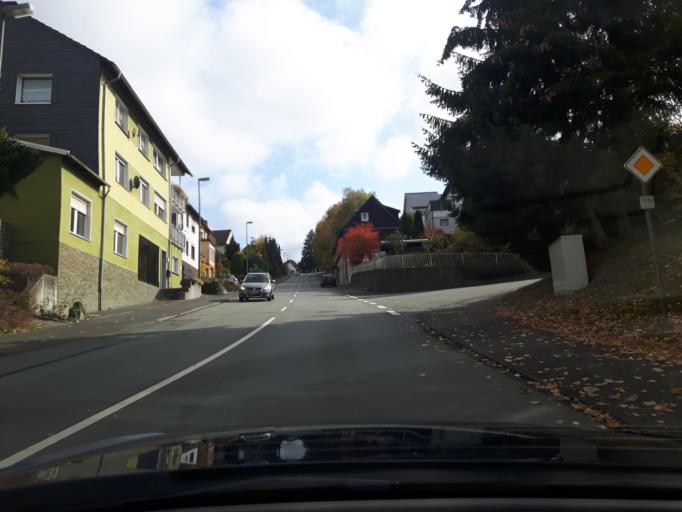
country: DE
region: North Rhine-Westphalia
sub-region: Regierungsbezirk Arnsberg
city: Bad Berleburg
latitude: 51.0453
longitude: 8.3944
